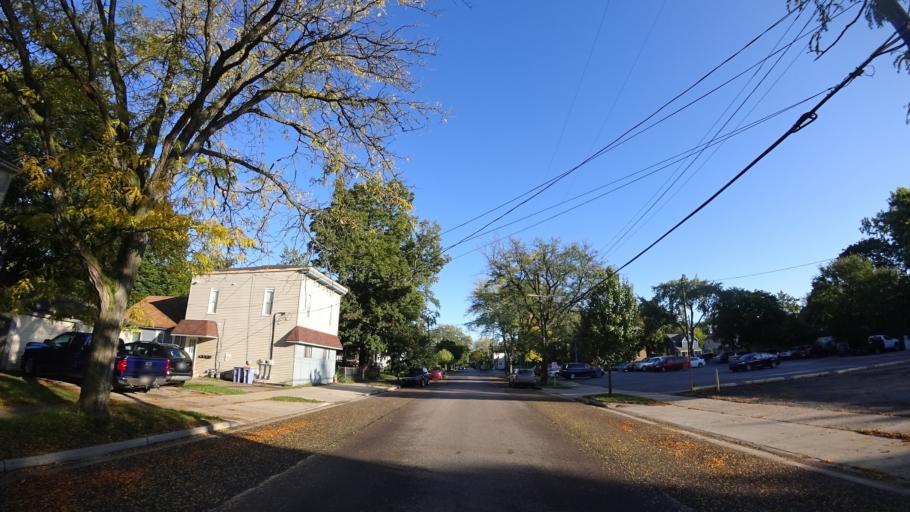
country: US
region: Michigan
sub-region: Kent County
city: Grand Rapids
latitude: 42.9929
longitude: -85.6646
